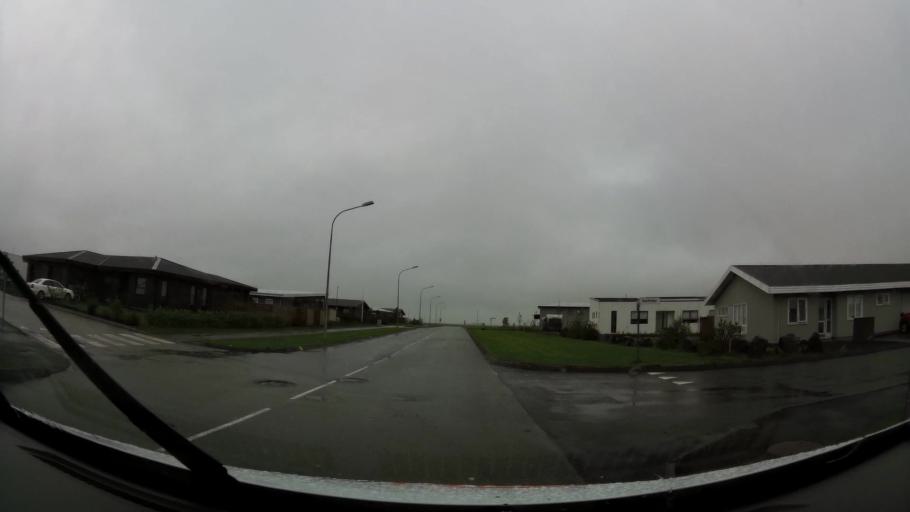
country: IS
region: South
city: Selfoss
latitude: 63.9254
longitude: -21.0082
